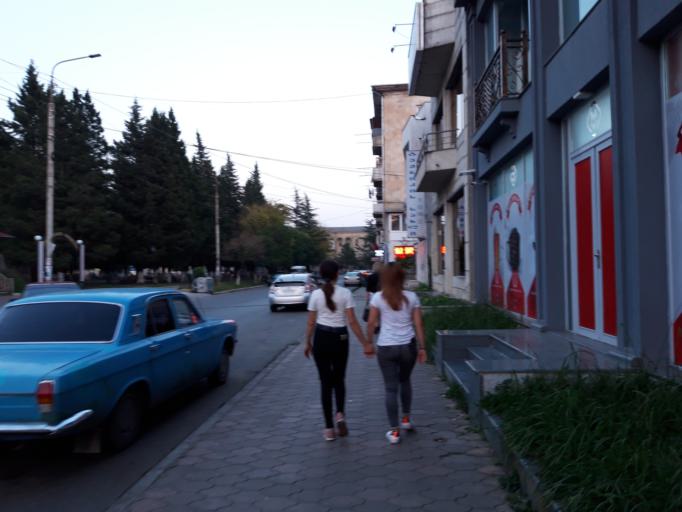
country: GE
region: Imereti
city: Samtredia
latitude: 42.1642
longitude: 42.3450
